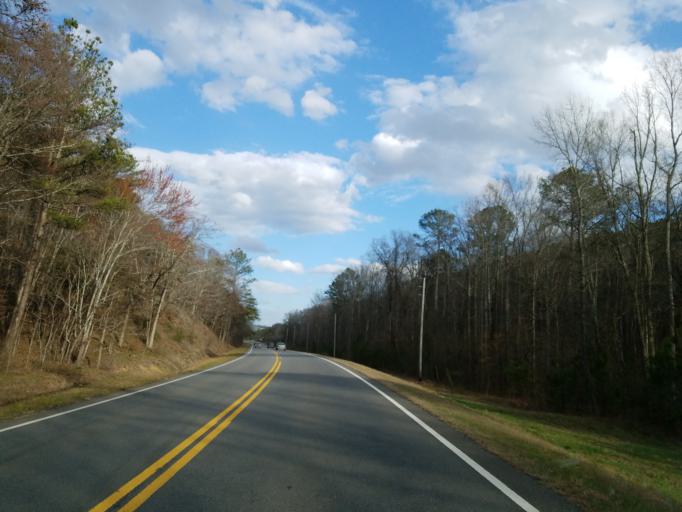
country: US
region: Georgia
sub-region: Bartow County
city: Rydal
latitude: 34.4471
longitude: -84.7526
